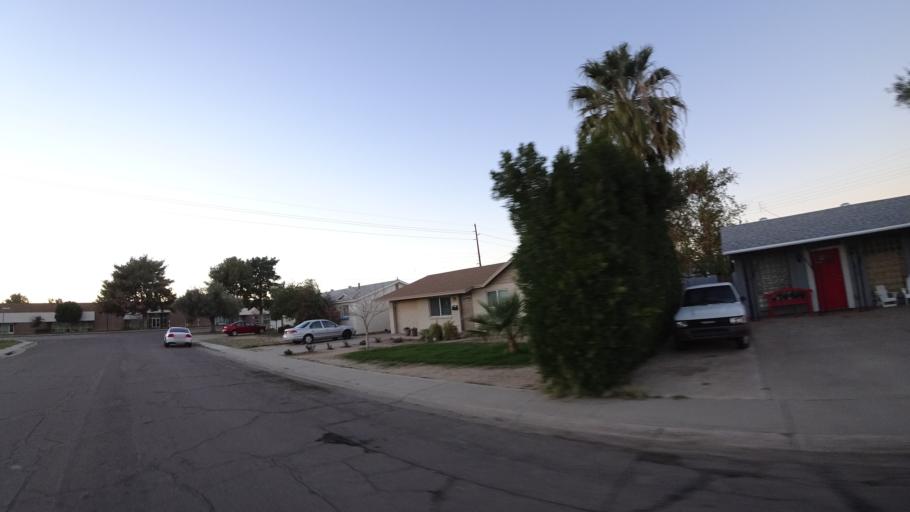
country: US
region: Arizona
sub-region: Maricopa County
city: Tempe Junction
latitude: 33.4180
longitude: -111.9602
